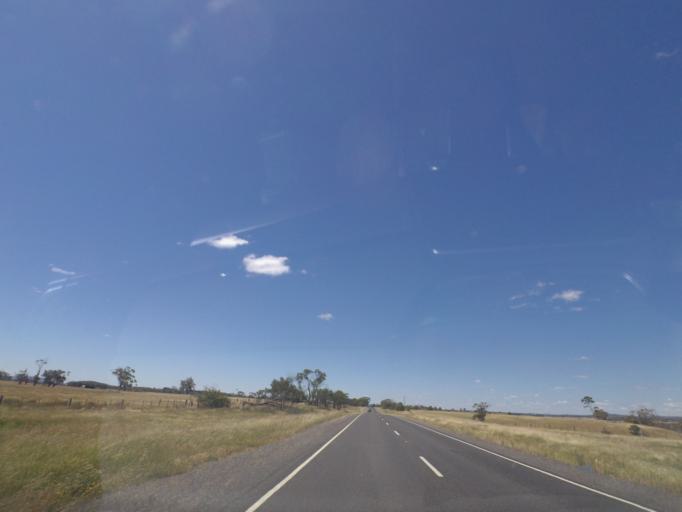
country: AU
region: Victoria
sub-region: Mount Alexander
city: Castlemaine
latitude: -37.2245
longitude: 144.3393
